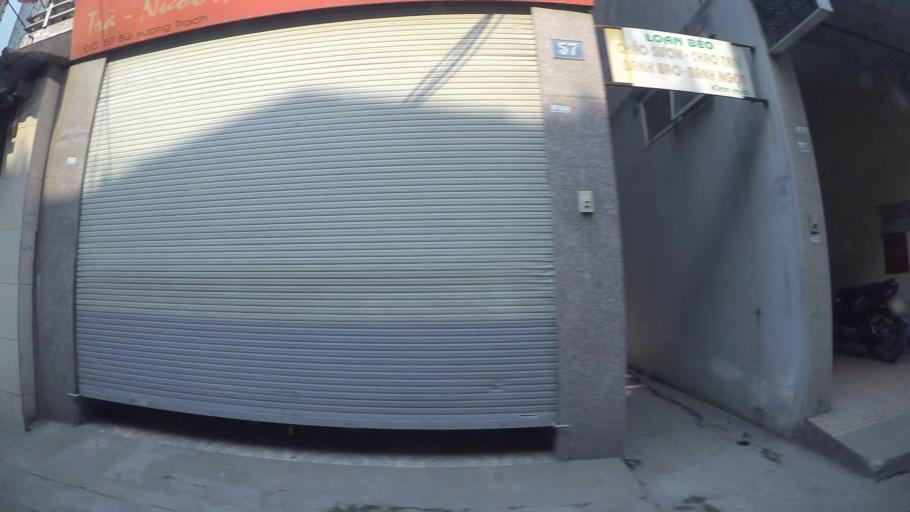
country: VN
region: Ha Noi
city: Thanh Xuan
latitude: 20.9908
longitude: 105.8175
